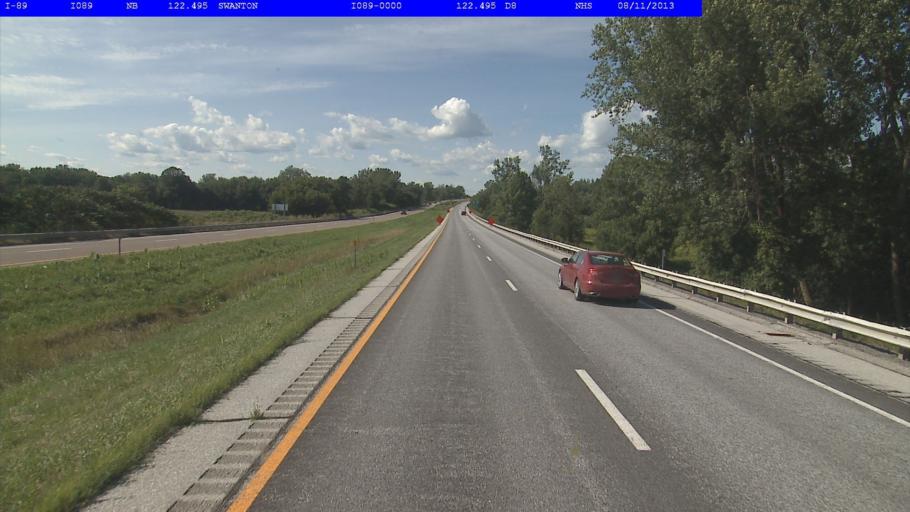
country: US
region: Vermont
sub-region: Franklin County
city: Swanton
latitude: 44.9105
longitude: -73.1006
